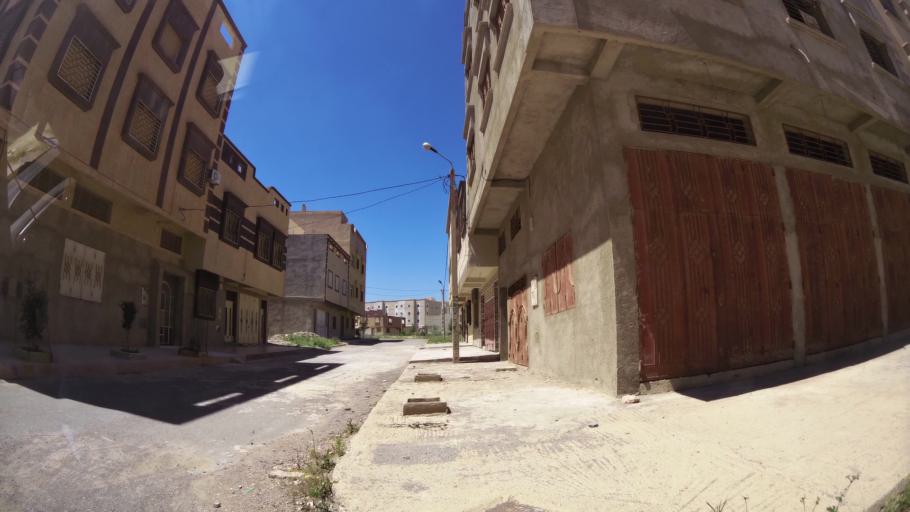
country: MA
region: Oriental
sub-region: Oujda-Angad
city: Oujda
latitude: 34.6605
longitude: -1.9475
